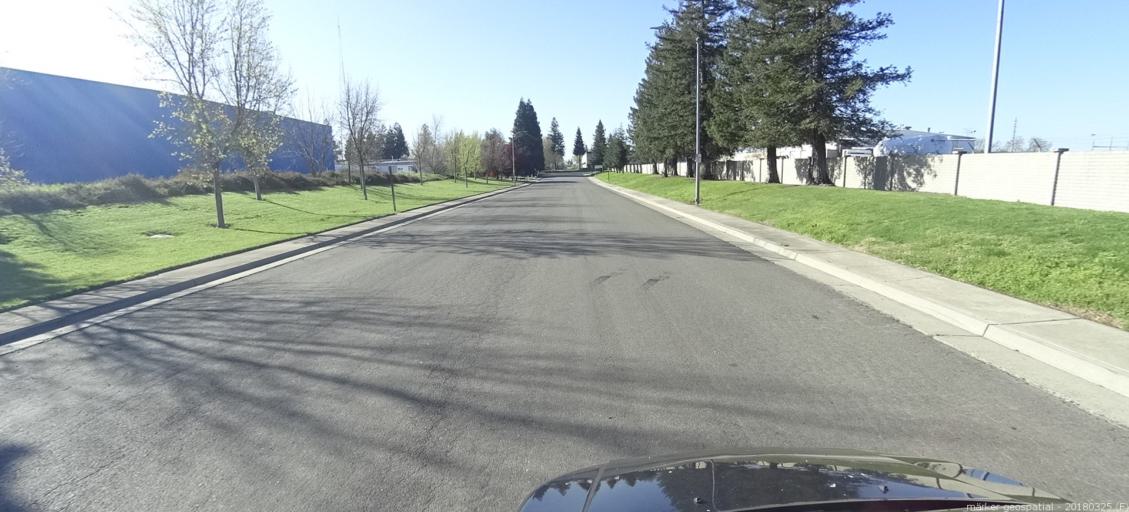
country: US
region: California
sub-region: Sacramento County
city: Rio Linda
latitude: 38.6532
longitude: -121.4810
